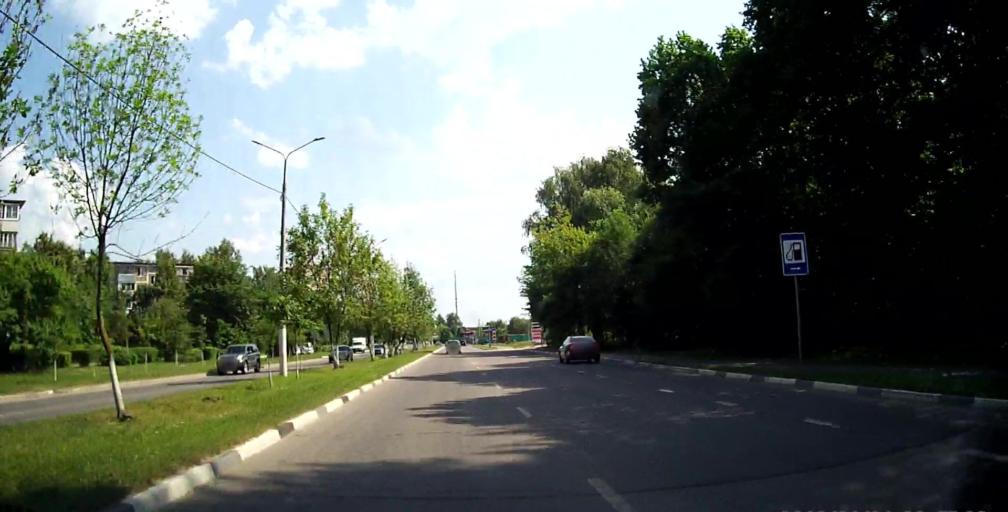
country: RU
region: Moskovskaya
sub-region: Podol'skiy Rayon
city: Podol'sk
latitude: 55.4138
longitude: 37.5221
